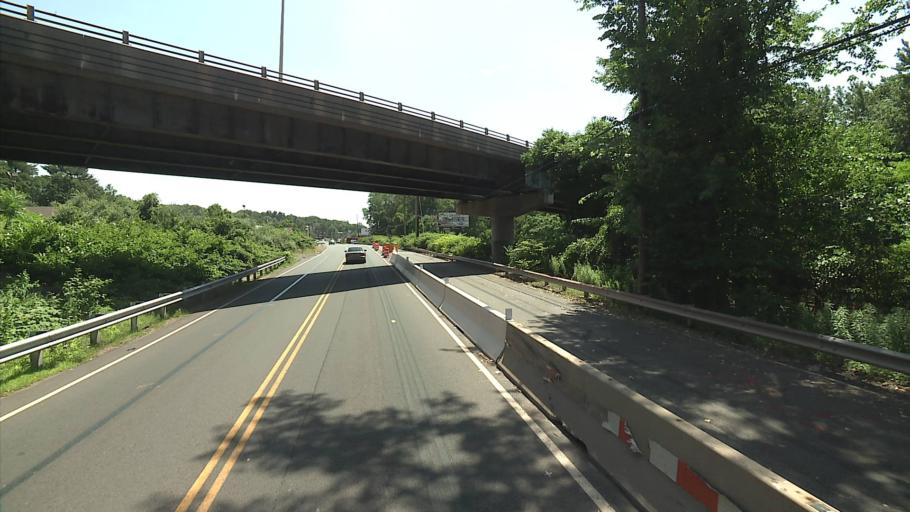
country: US
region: Connecticut
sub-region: Hartford County
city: Plainville
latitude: 41.6686
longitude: -72.8214
